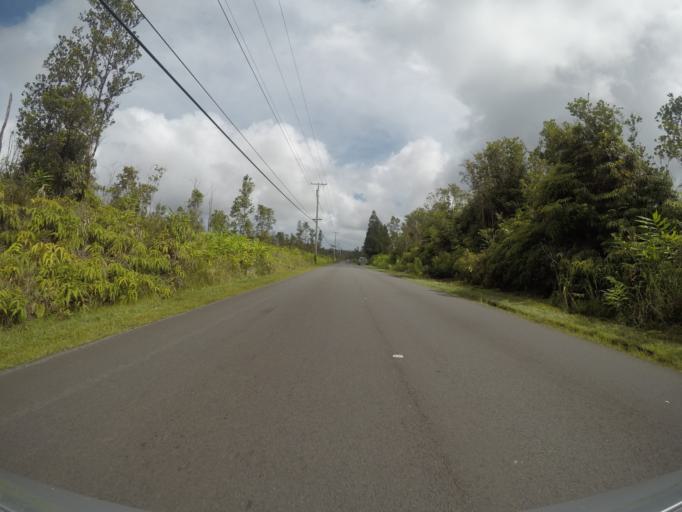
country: US
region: Hawaii
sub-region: Hawaii County
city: Fern Acres
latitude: 19.4766
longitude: -155.1410
